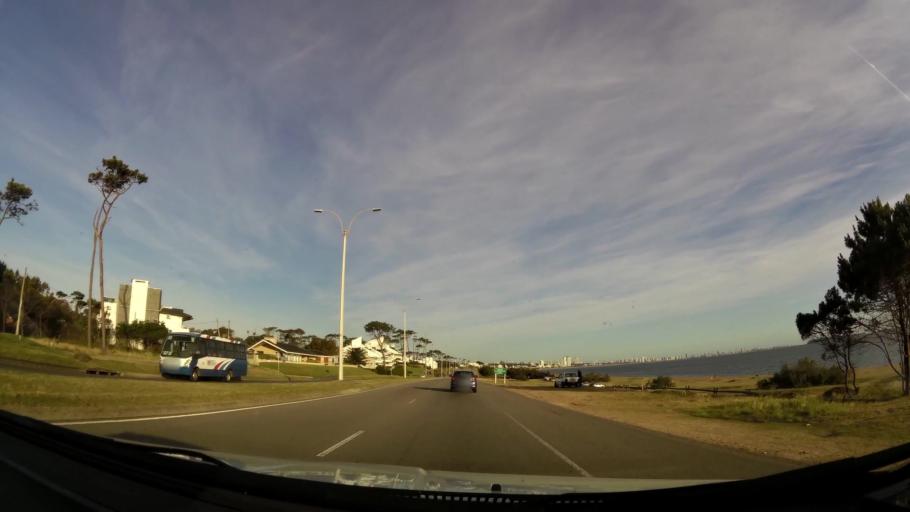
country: UY
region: Maldonado
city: Maldonado
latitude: -34.9108
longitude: -54.9946
